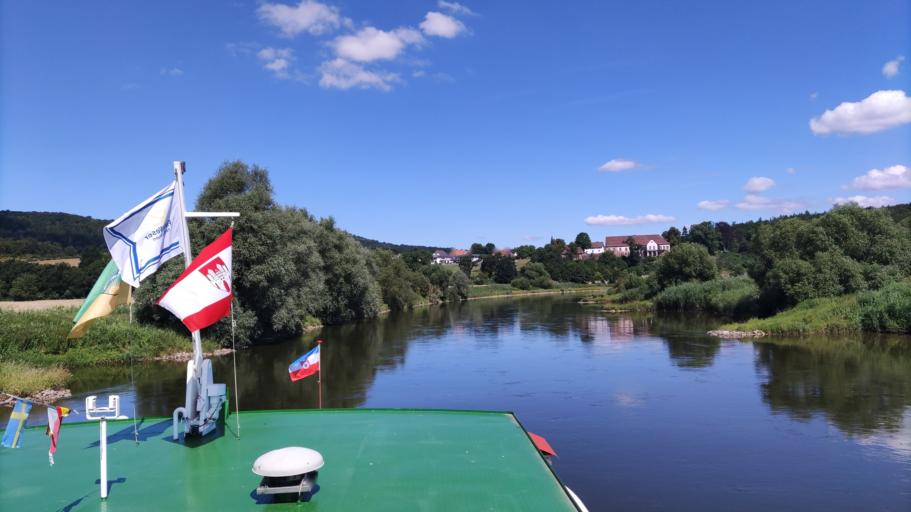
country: DE
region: North Rhine-Westphalia
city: Beverungen
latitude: 51.6879
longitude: 9.3897
